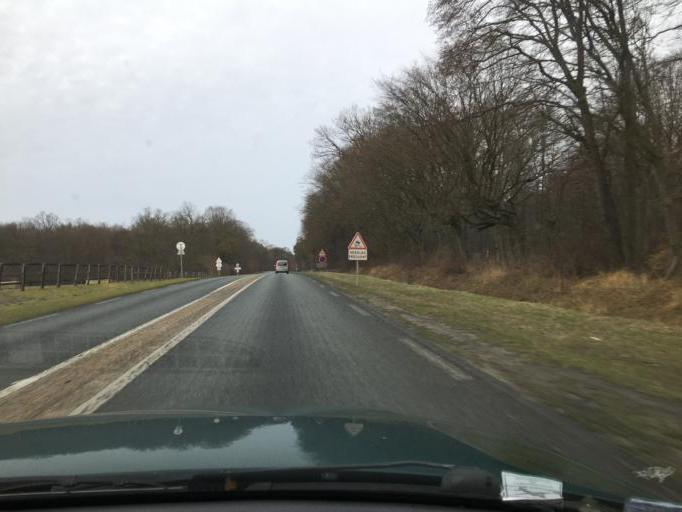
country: FR
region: Picardie
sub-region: Departement de l'Oise
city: Thiers-sur-Theve
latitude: 49.1573
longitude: 2.5514
